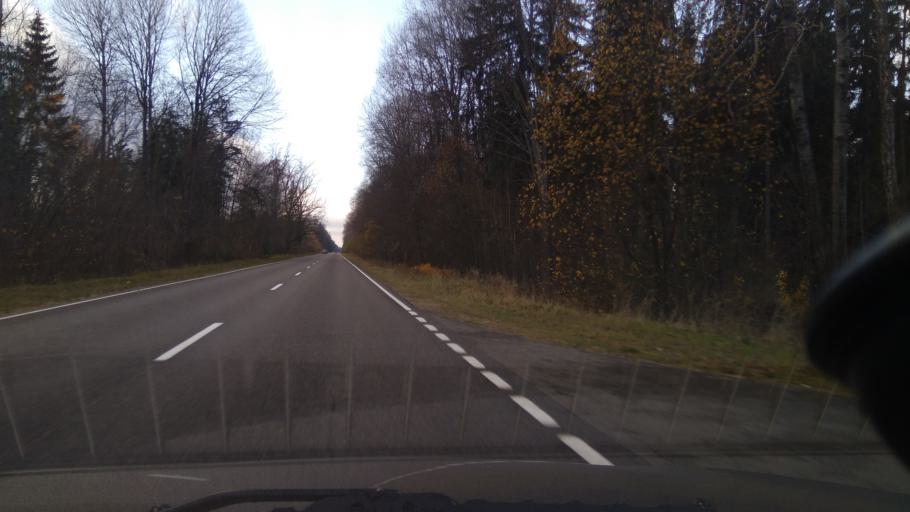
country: BY
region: Minsk
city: Urechcha
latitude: 53.2104
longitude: 27.8953
